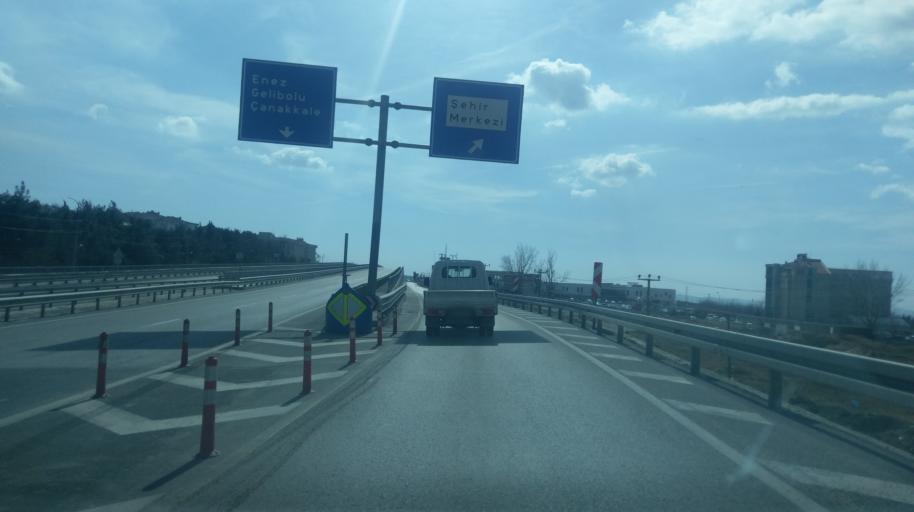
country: TR
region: Edirne
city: Kesan
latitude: 40.8617
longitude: 26.6216
